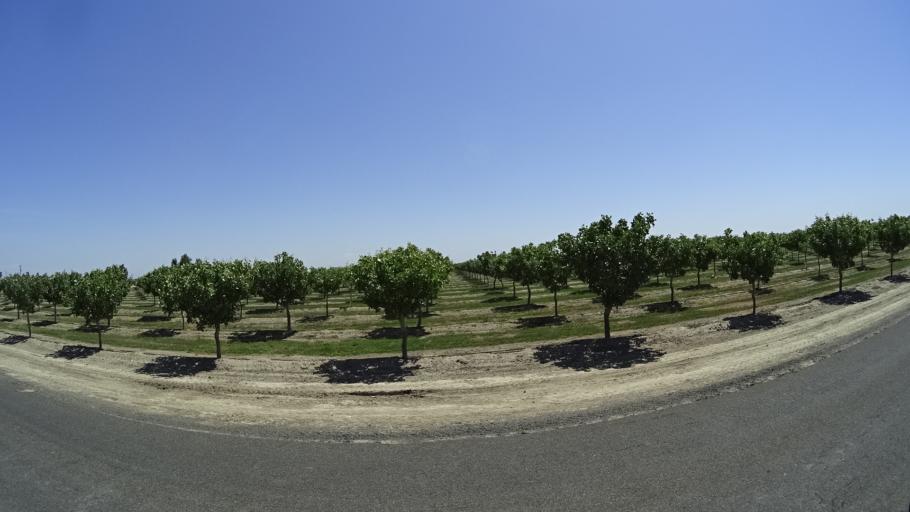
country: US
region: California
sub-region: Kings County
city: Lemoore
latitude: 36.2528
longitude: -119.7446
